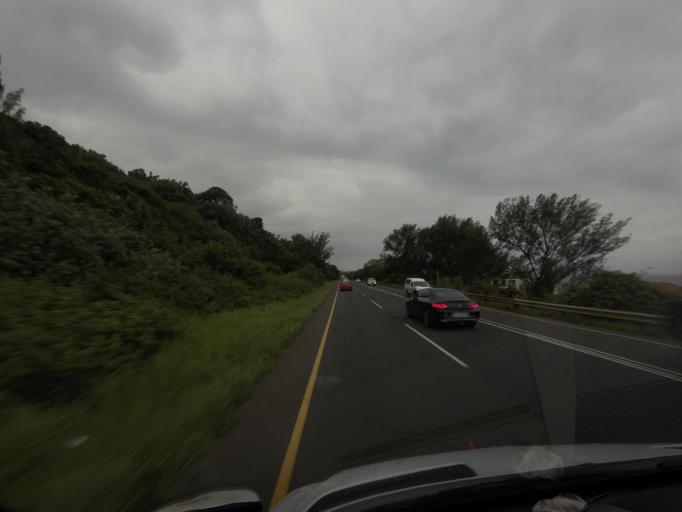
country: ZA
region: KwaZulu-Natal
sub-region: iLembe District Municipality
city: Ballitoville
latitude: -29.5877
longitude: 31.1724
